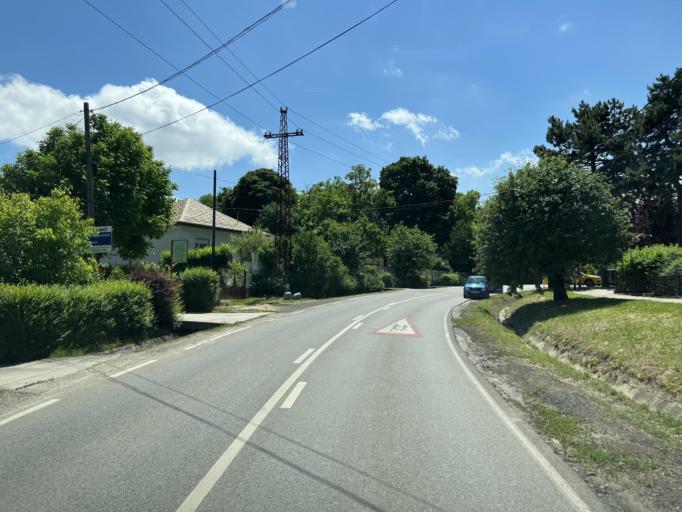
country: HU
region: Pest
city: Csomor
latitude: 47.5465
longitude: 19.2208
